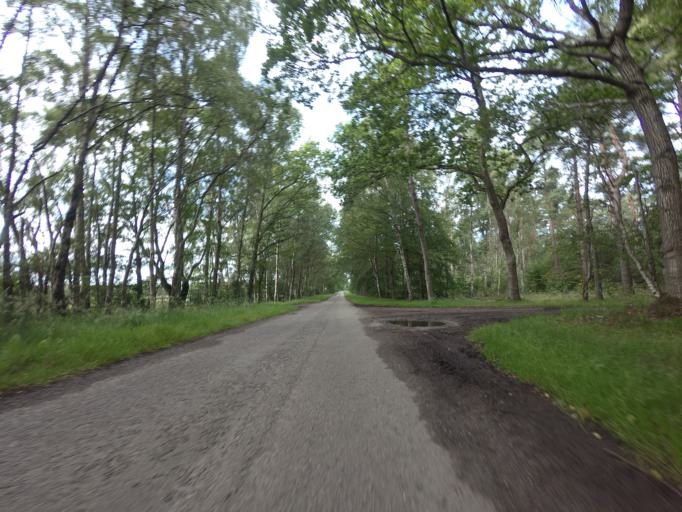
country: GB
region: Scotland
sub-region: Moray
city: Hopeman
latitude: 57.6690
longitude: -3.4178
